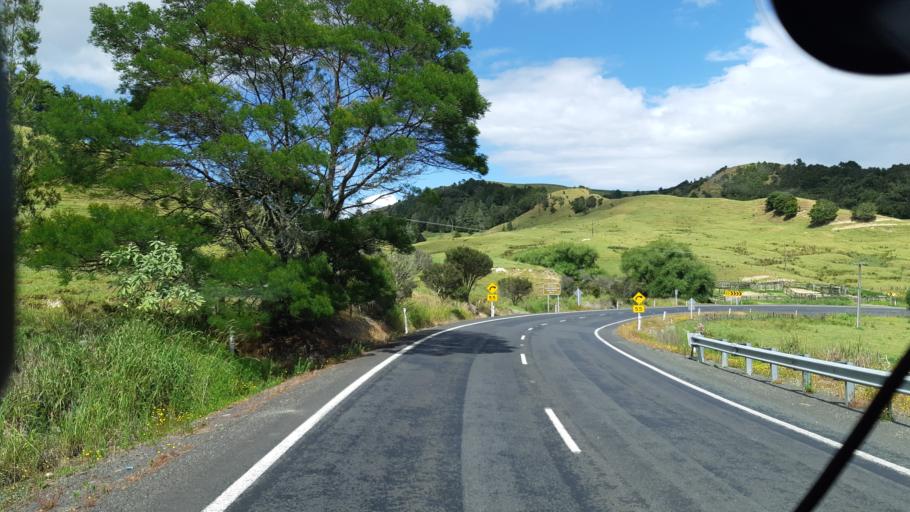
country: NZ
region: Northland
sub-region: Far North District
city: Taipa
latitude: -35.2456
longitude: 173.5484
